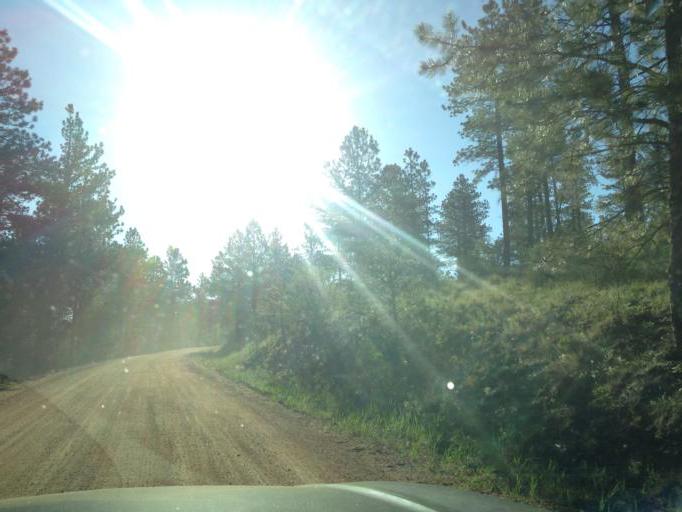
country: US
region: Colorado
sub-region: Jefferson County
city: Evergreen
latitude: 39.4059
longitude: -105.5053
